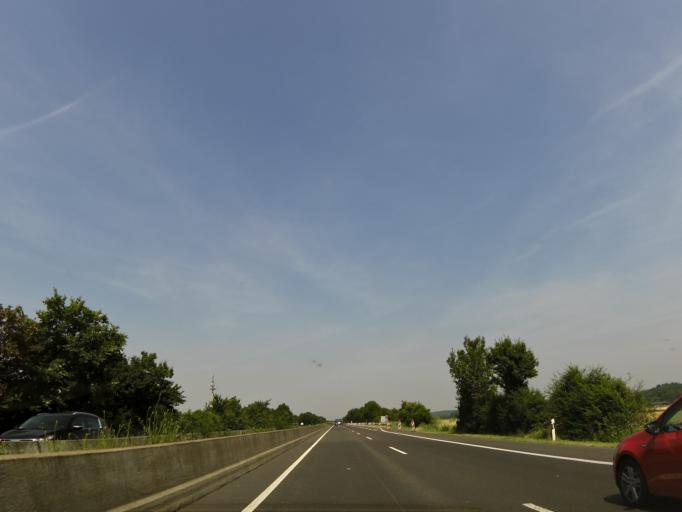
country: DE
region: North Rhine-Westphalia
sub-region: Regierungsbezirk Koln
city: Weilerswist
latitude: 50.7338
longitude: 6.8780
